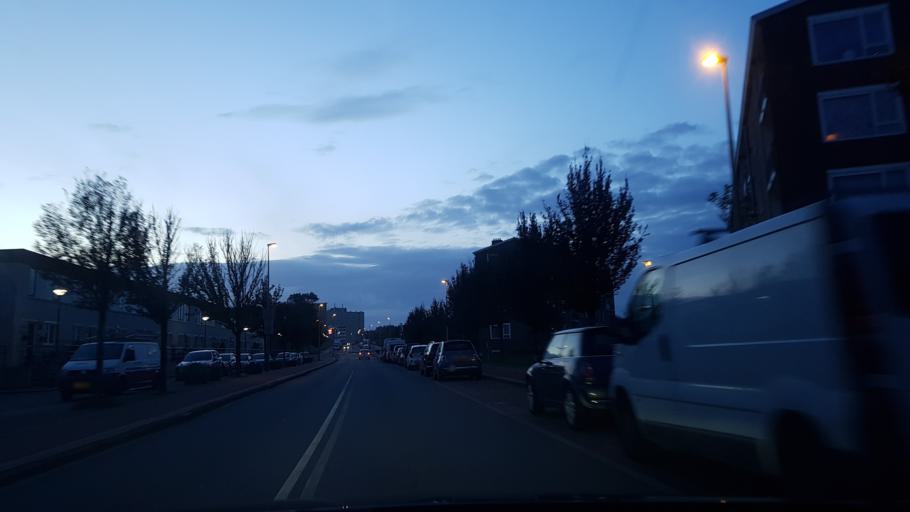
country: NL
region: North Holland
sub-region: Gemeente Zandvoort
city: Zandvoort
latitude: 52.3778
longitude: 4.5396
